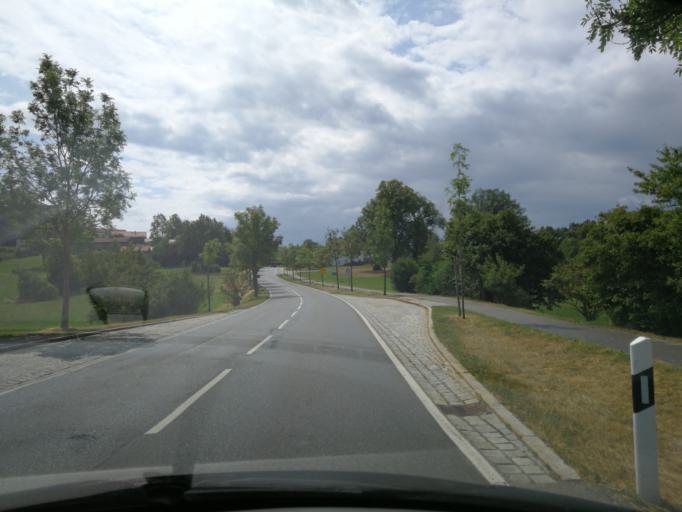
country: DE
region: Bavaria
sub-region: Upper Palatinate
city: Brennberg
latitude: 49.0761
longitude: 12.3937
